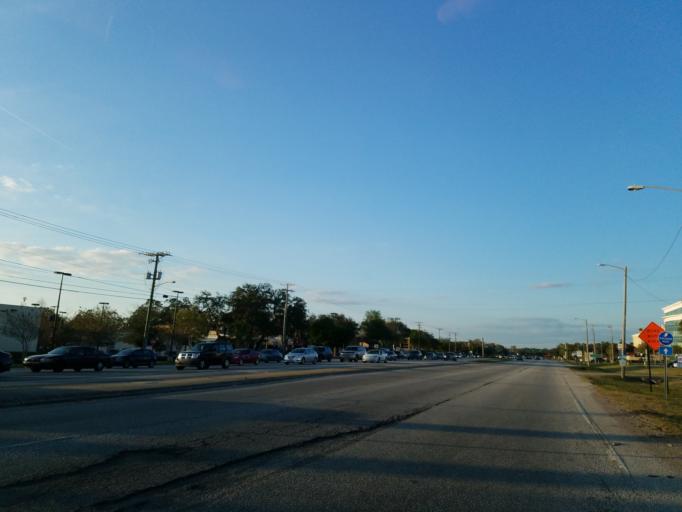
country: US
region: Florida
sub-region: Hillsborough County
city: University
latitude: 28.0694
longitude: -82.4259
